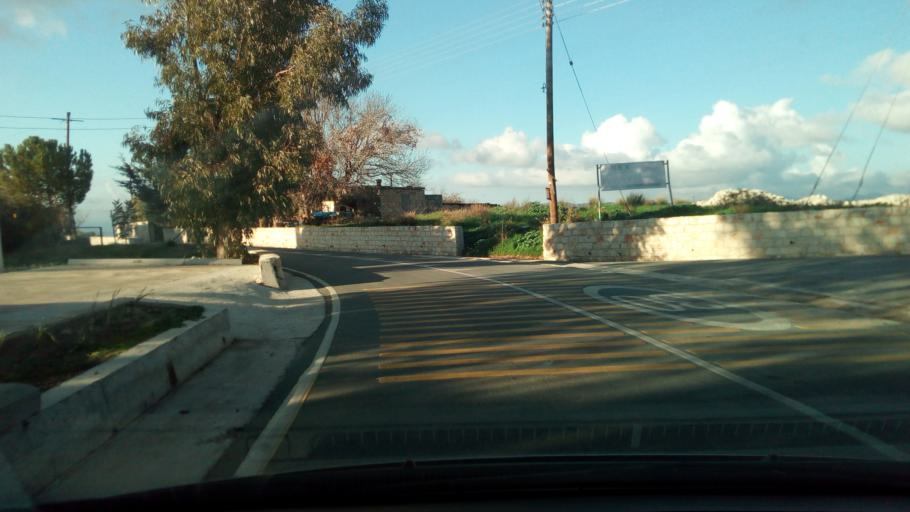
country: CY
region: Pafos
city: Tala
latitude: 34.9254
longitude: 32.5251
